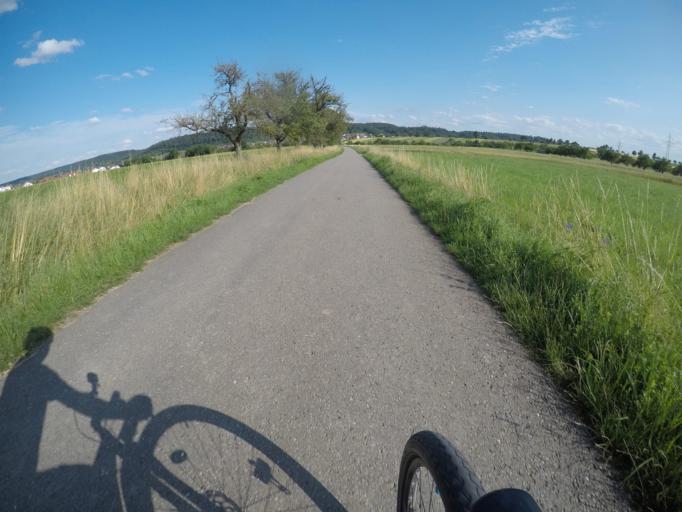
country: DE
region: Baden-Wuerttemberg
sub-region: Regierungsbezirk Stuttgart
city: Nufringen
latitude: 48.6234
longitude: 8.8752
